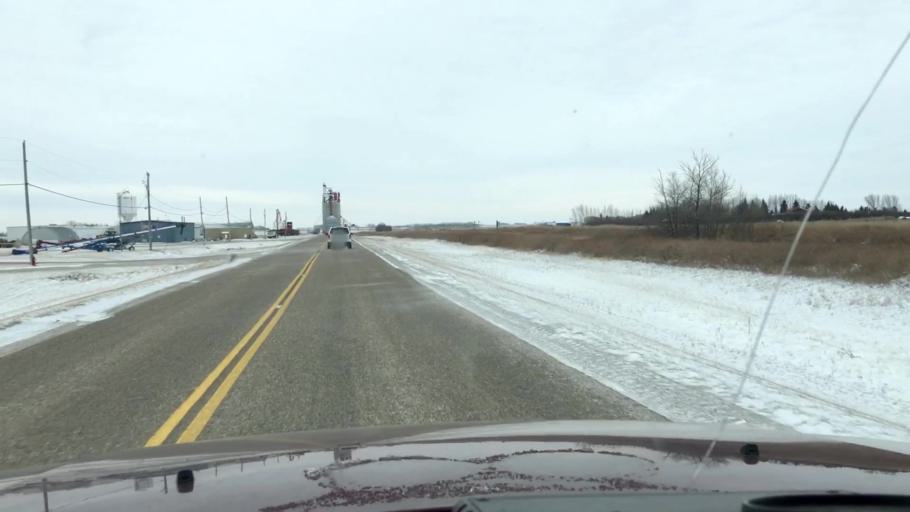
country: CA
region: Saskatchewan
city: Watrous
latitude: 51.2544
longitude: -105.9831
